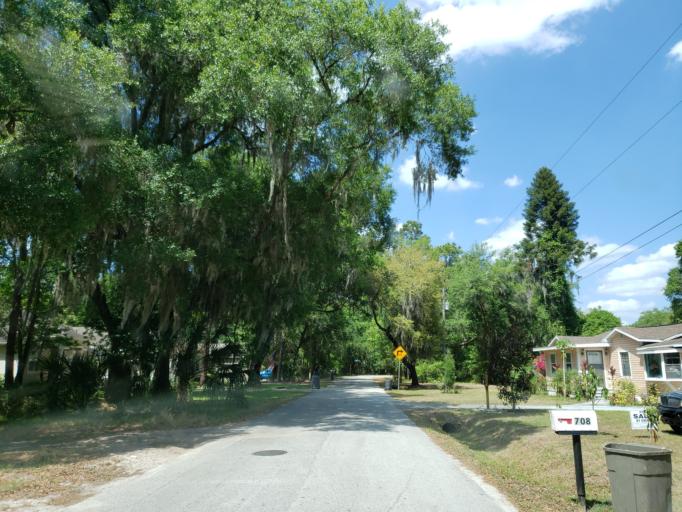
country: US
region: Florida
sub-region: Hillsborough County
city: Plant City
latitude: 28.0210
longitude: -82.1331
